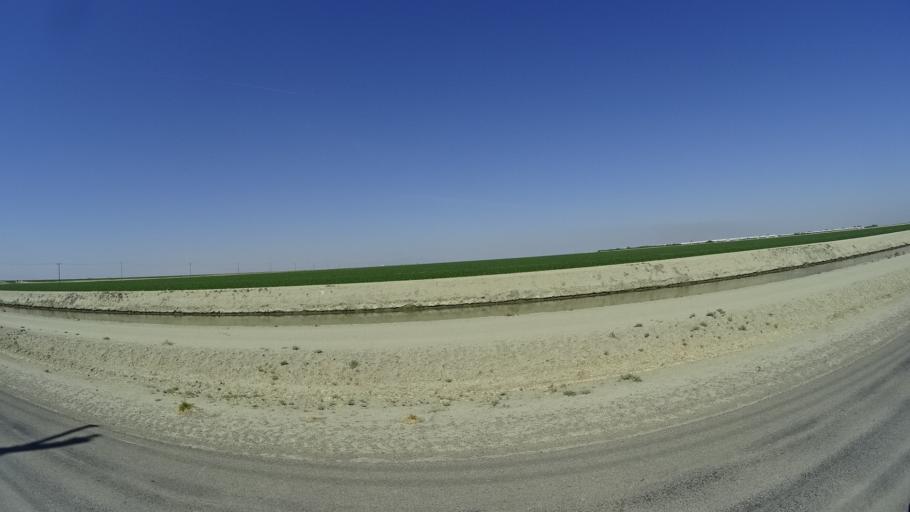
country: US
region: California
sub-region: Kings County
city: Corcoran
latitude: 35.9947
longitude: -119.5361
